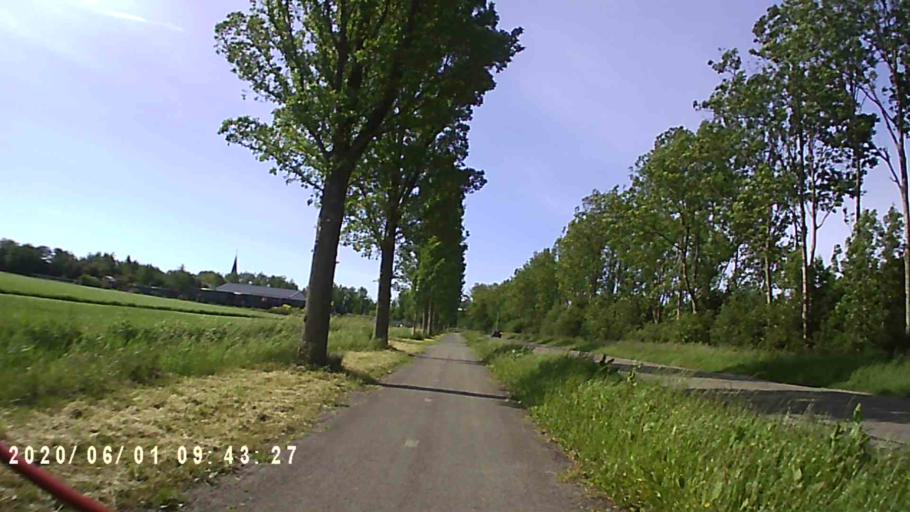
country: NL
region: Friesland
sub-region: Menameradiel
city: Menaam
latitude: 53.2407
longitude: 5.6837
